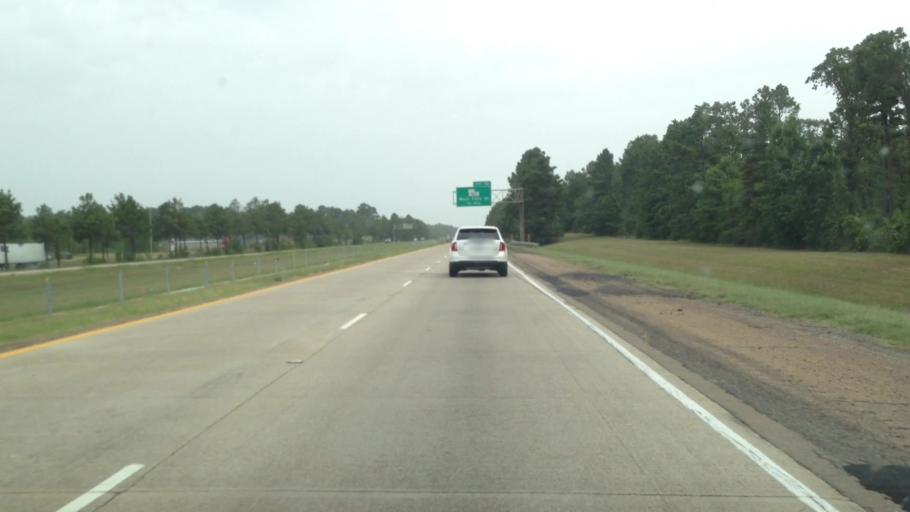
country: US
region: Louisiana
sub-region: Caddo Parish
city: Shreveport
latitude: 32.4308
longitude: -93.8396
